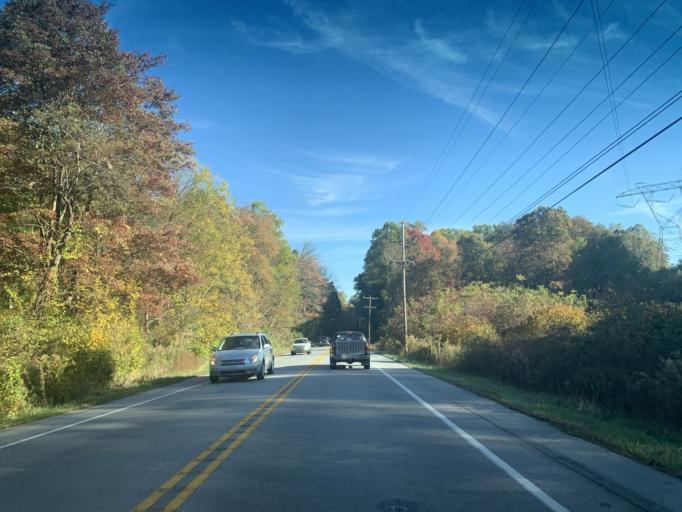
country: US
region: Pennsylvania
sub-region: Chester County
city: Parkesburg
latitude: 39.9472
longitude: -75.9145
